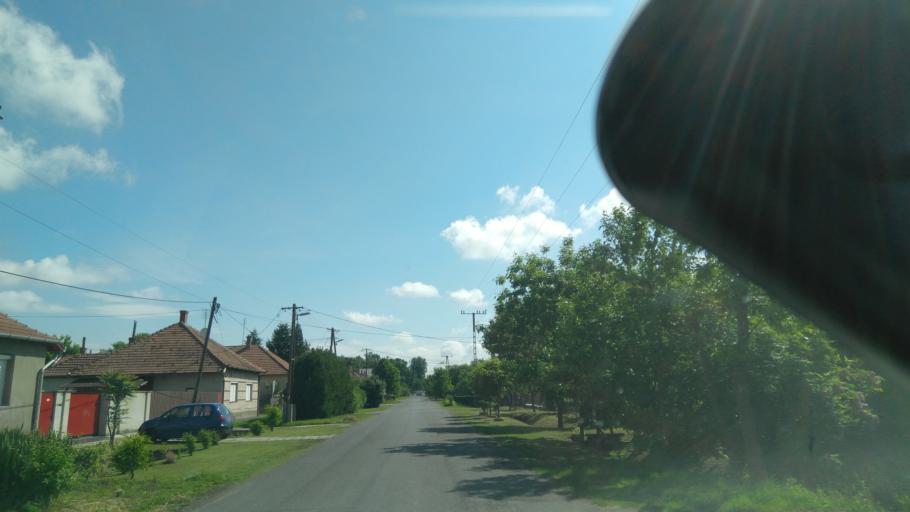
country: HU
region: Bekes
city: Bekes
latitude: 46.7748
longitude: 21.1149
